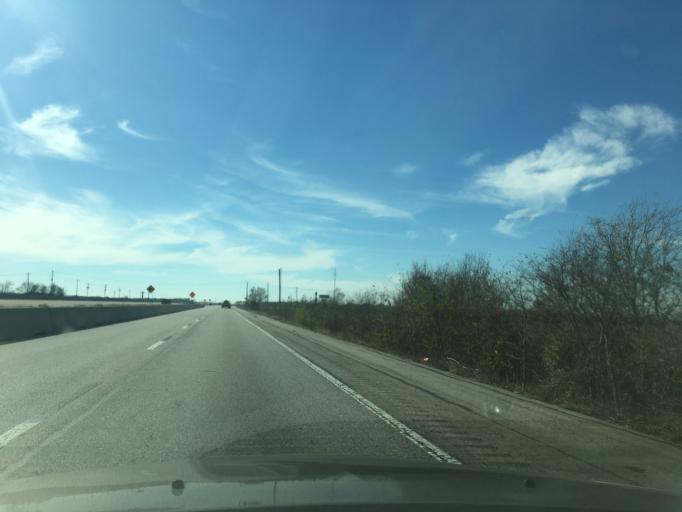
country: US
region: Texas
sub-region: Wharton County
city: East Bernard
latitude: 29.4798
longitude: -95.9467
